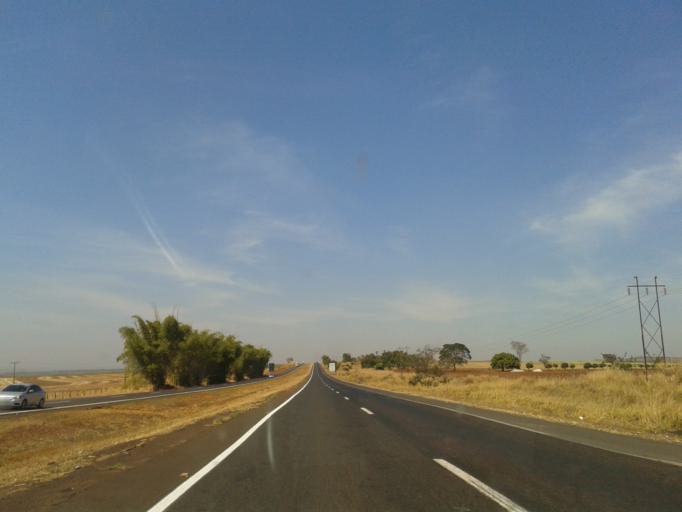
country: BR
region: Goias
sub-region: Goiatuba
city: Goiatuba
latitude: -18.2029
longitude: -49.2797
